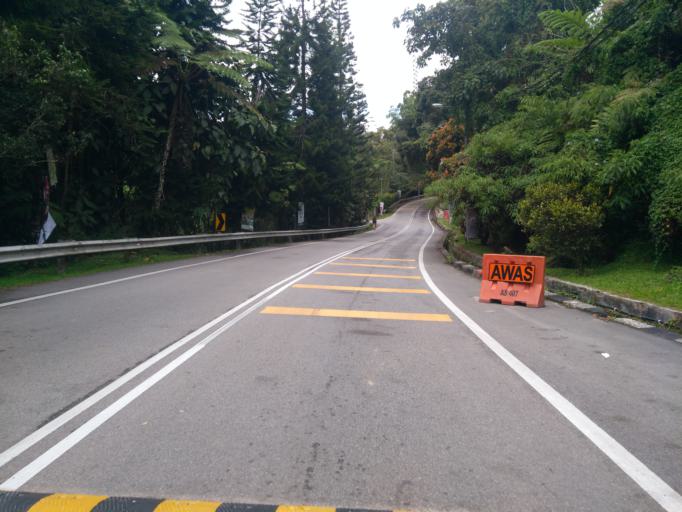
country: MY
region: Pahang
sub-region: Cameron Highlands
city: Tanah Rata
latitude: 4.4755
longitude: 101.3816
